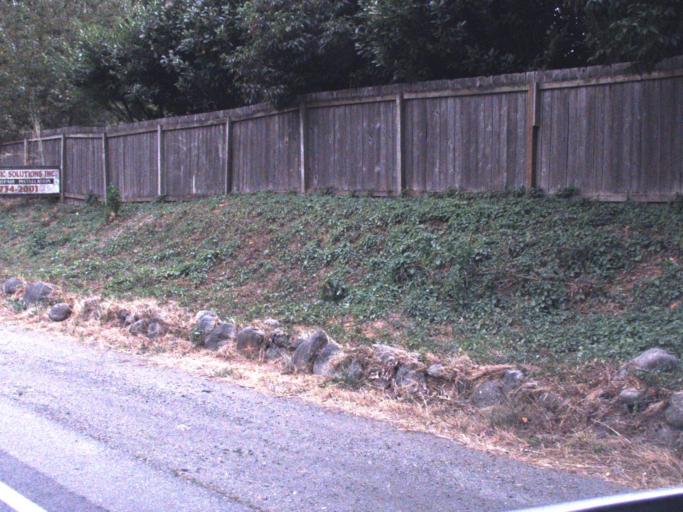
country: US
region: Washington
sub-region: King County
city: Carnation
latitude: 47.6147
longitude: -121.9103
